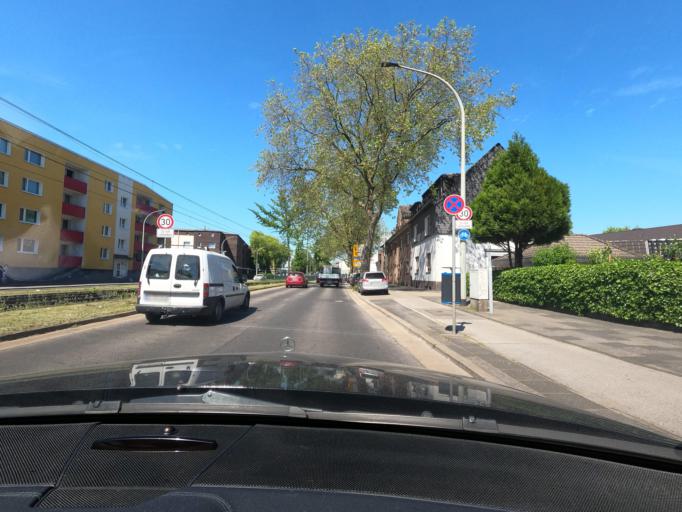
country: DE
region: North Rhine-Westphalia
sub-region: Regierungsbezirk Dusseldorf
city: Hochfeld
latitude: 51.4044
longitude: 6.7643
